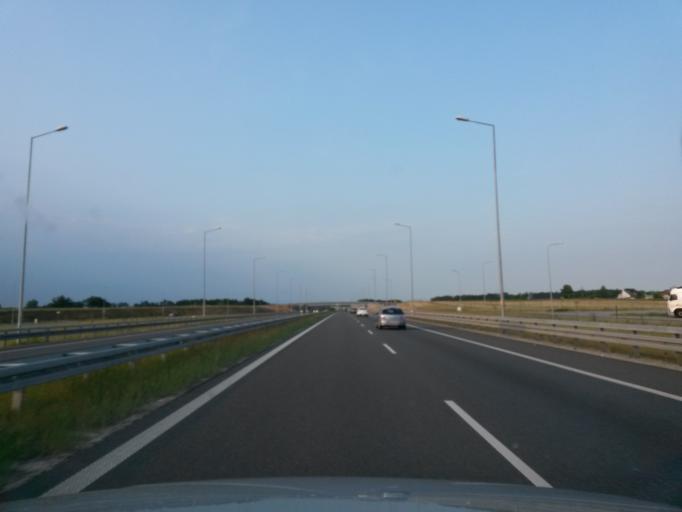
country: PL
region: Lower Silesian Voivodeship
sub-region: Powiat olesnicki
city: Olesnica
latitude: 51.2401
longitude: 17.4995
